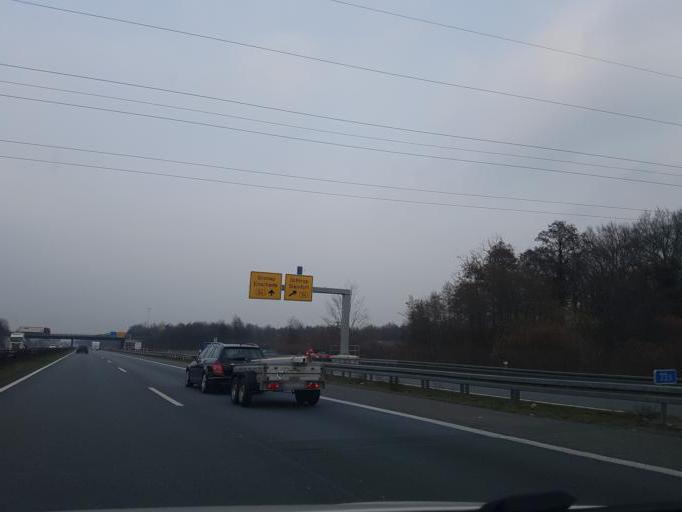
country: DE
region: North Rhine-Westphalia
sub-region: Regierungsbezirk Munster
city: Heek
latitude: 52.1893
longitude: 7.1143
